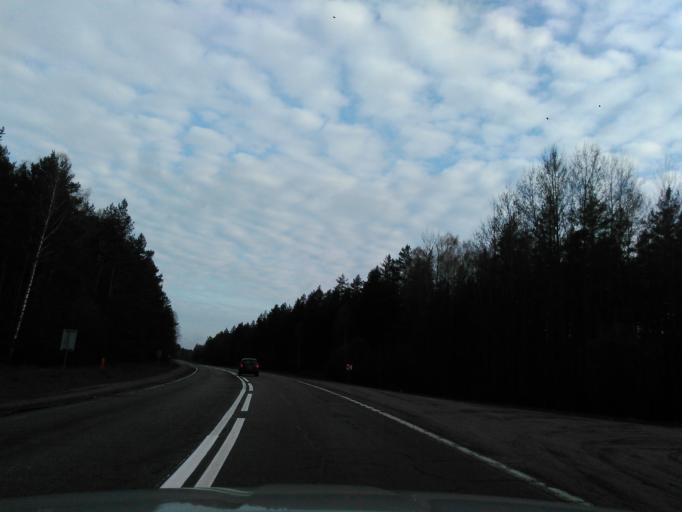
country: BY
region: Minsk
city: Plyeshchanitsy
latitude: 54.3833
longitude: 27.8737
